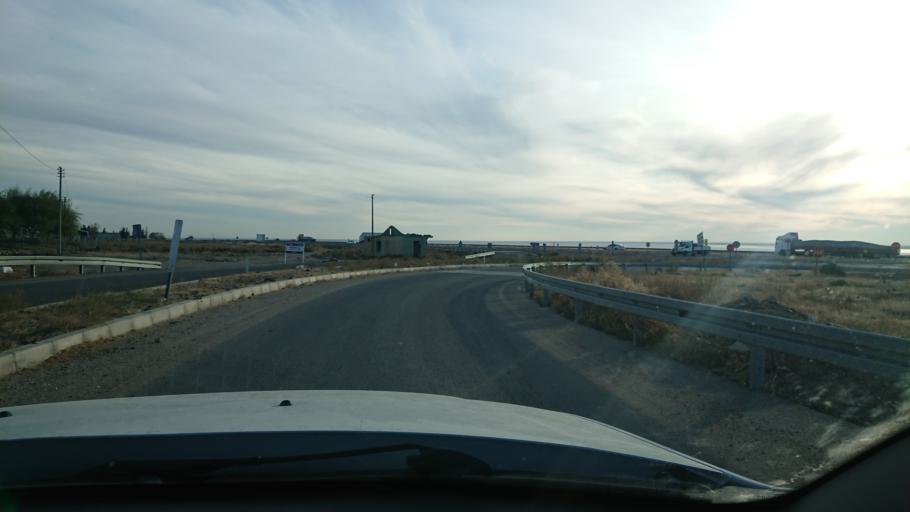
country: TR
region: Ankara
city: Sereflikochisar
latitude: 38.7406
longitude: 33.6661
